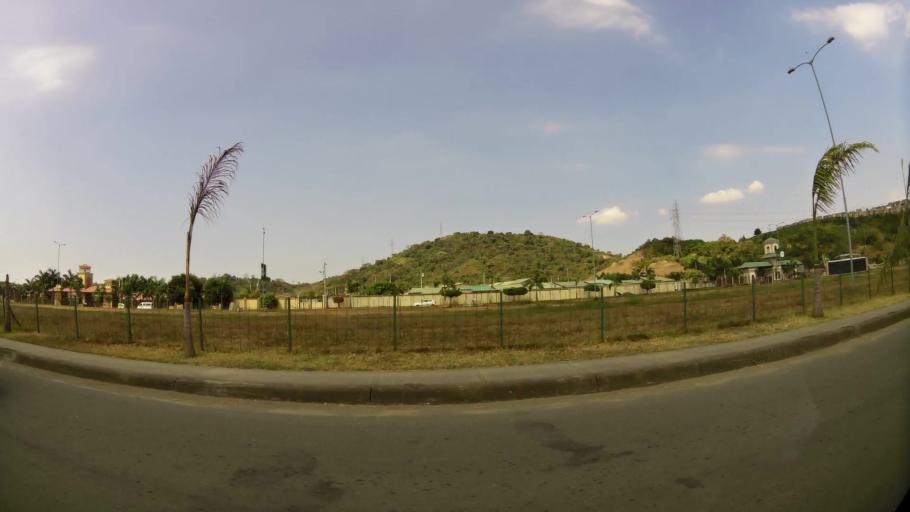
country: EC
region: Guayas
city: El Triunfo
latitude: -2.0334
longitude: -79.9149
